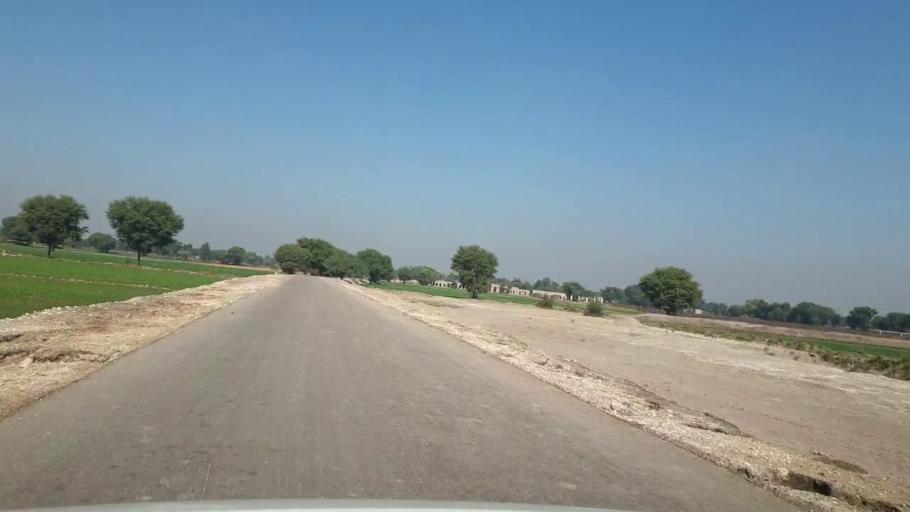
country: PK
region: Sindh
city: Johi
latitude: 26.6624
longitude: 67.7055
